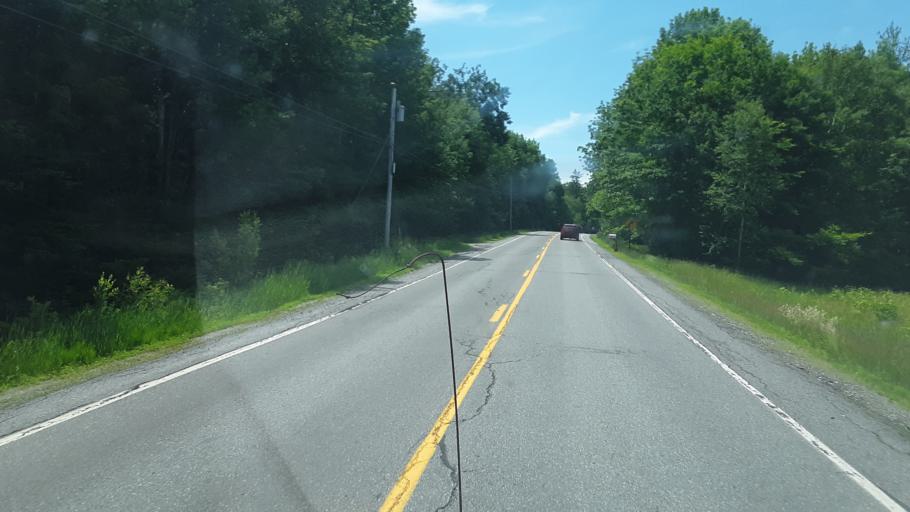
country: US
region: Maine
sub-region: Hancock County
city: Bucksport
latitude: 44.5627
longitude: -68.8399
